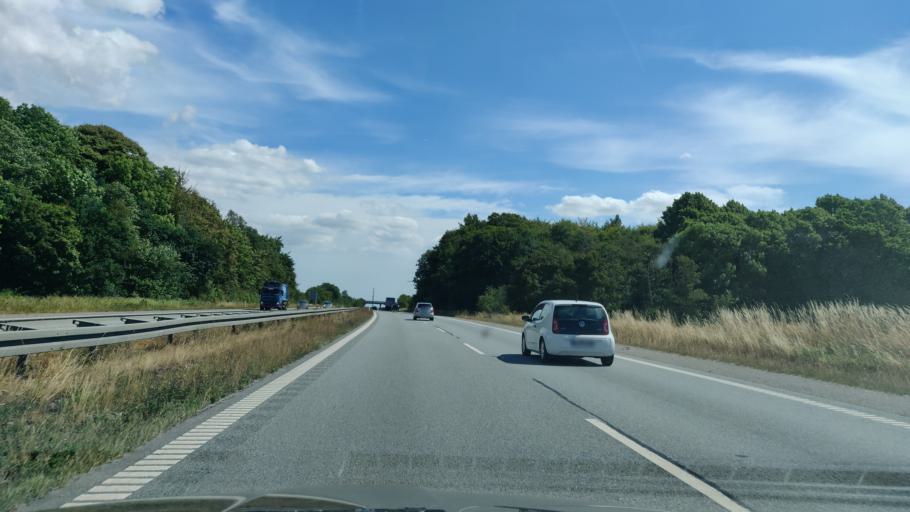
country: DK
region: Zealand
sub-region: Lejre Kommune
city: Lejre
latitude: 55.6425
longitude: 11.9428
